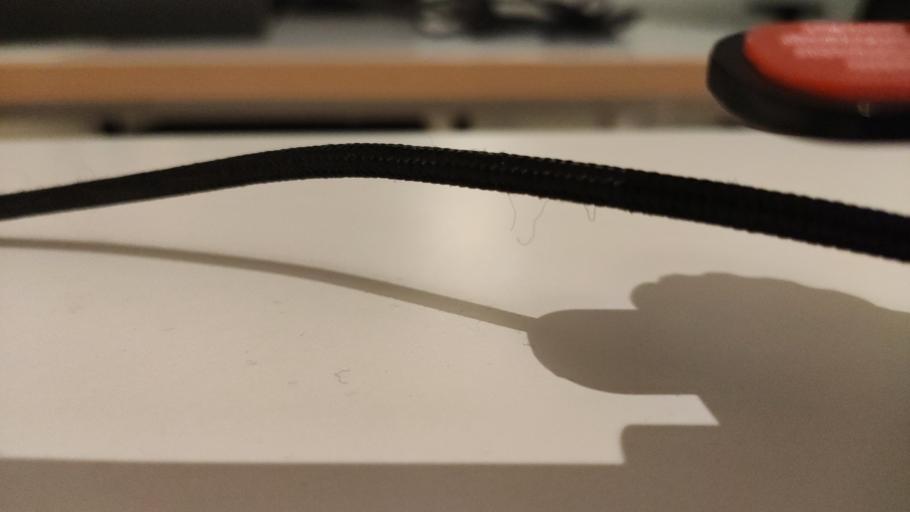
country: RU
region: Moskovskaya
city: Malaya Dubna
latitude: 55.8612
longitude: 38.9624
